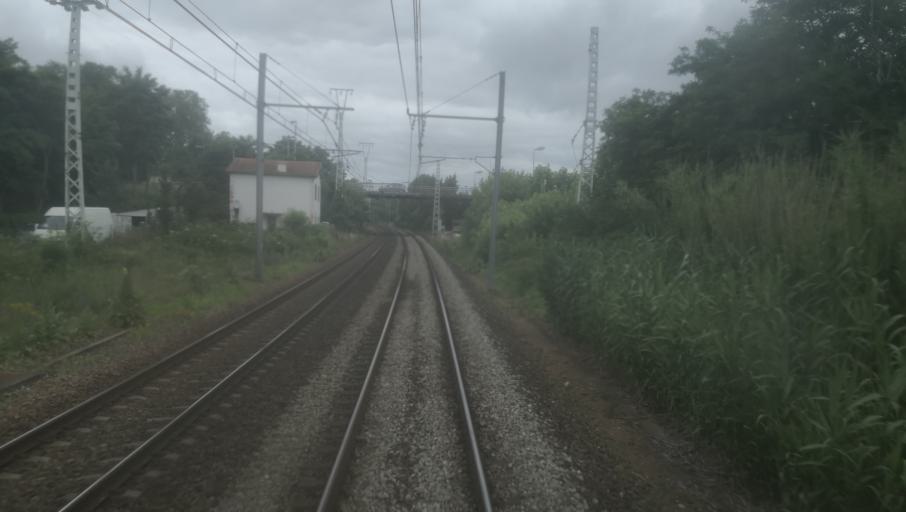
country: FR
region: Midi-Pyrenees
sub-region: Departement de la Haute-Garonne
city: Saint-Jory
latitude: 43.7397
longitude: 1.3704
